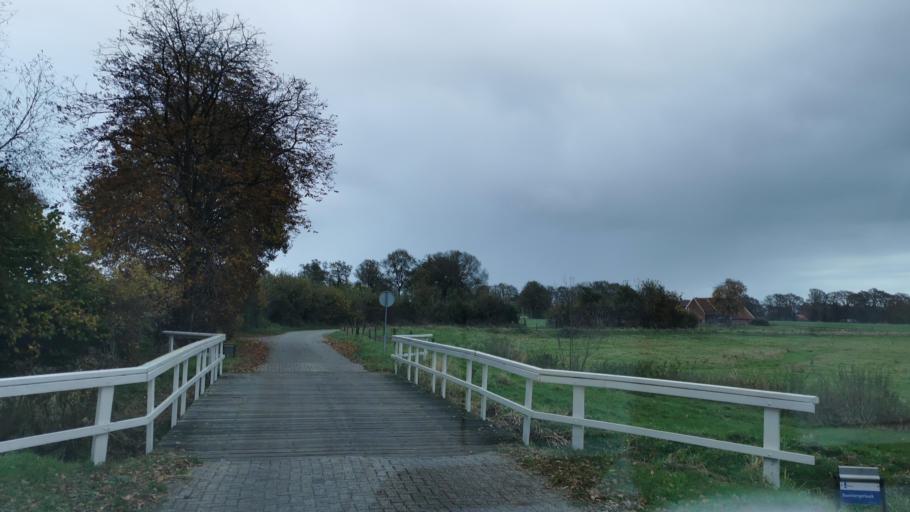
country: NL
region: Overijssel
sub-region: Gemeente Losser
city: Losser
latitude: 52.2504
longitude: 7.0285
